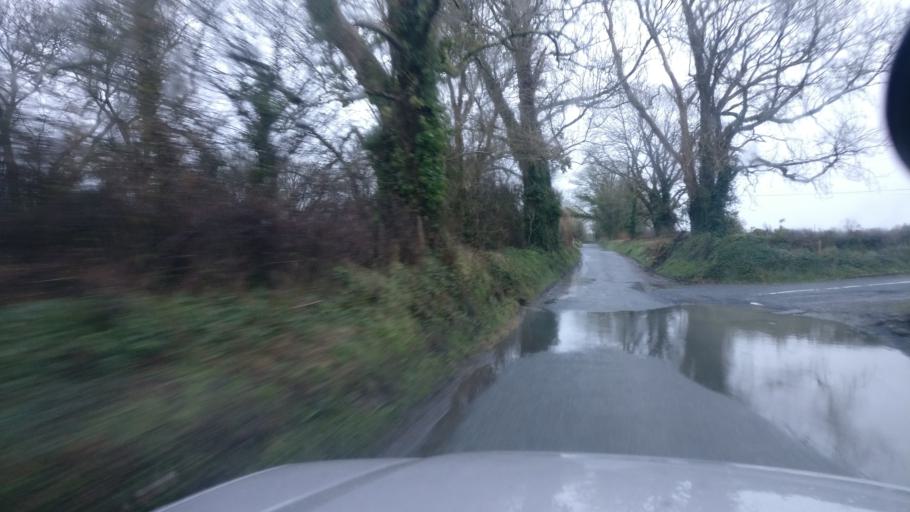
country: IE
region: Connaught
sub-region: County Galway
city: Ballinasloe
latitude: 53.3288
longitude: -8.3931
